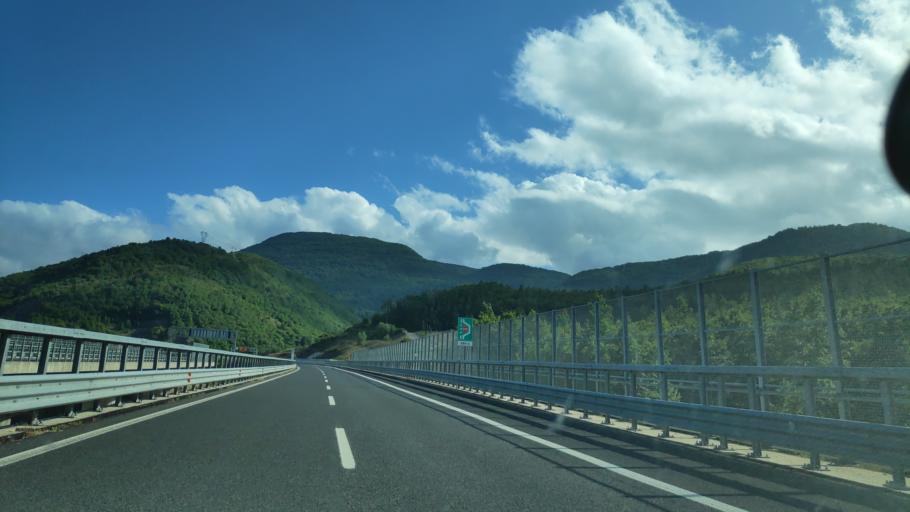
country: IT
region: Campania
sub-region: Provincia di Salerno
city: Casalbuono
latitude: 40.2203
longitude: 15.6718
